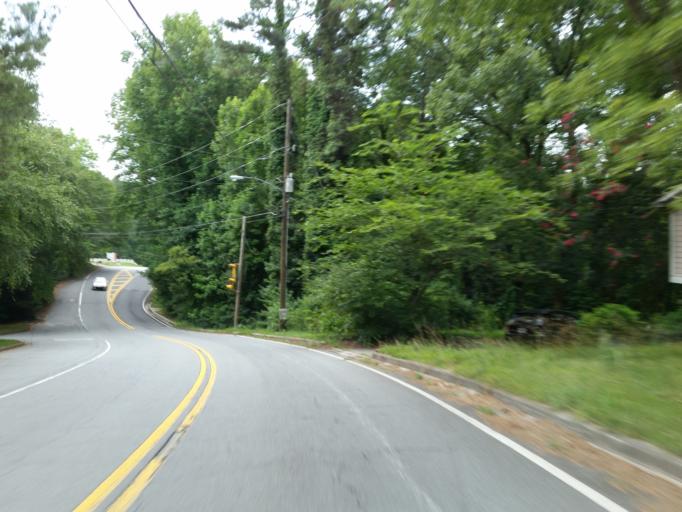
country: US
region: Georgia
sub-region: Cobb County
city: Marietta
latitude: 33.9935
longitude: -84.4777
